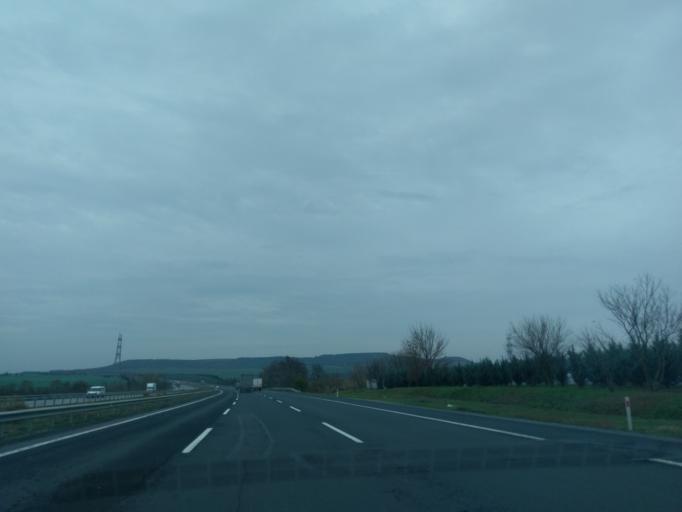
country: TR
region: Istanbul
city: Canta
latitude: 41.1504
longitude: 28.1454
